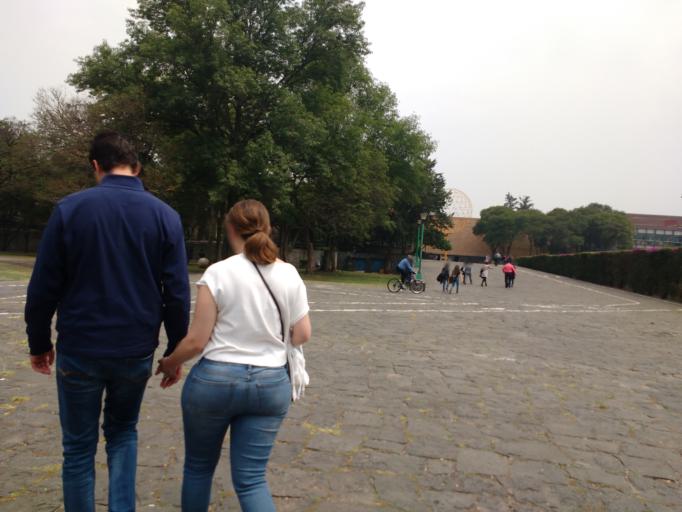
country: MX
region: Mexico City
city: Magdalena Contreras
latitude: 19.3327
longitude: -99.1868
